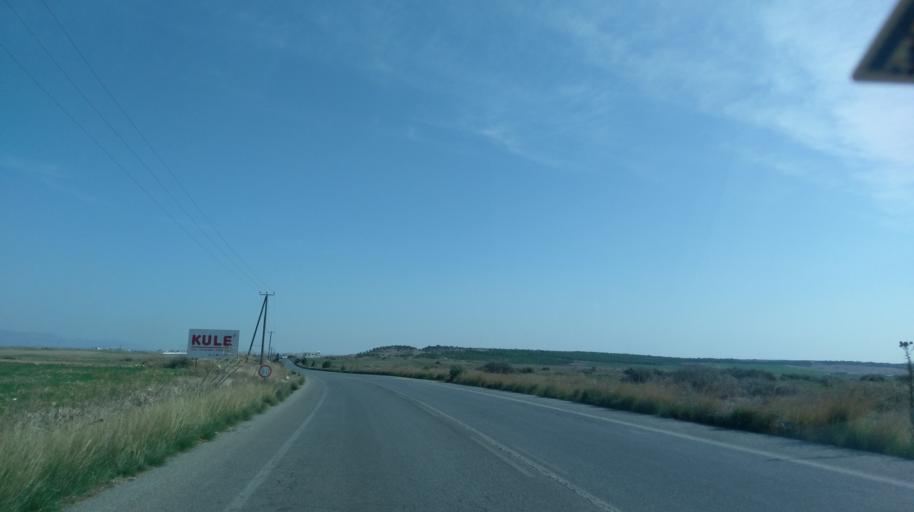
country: CY
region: Ammochostos
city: Lefkonoiko
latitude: 35.2340
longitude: 33.5676
